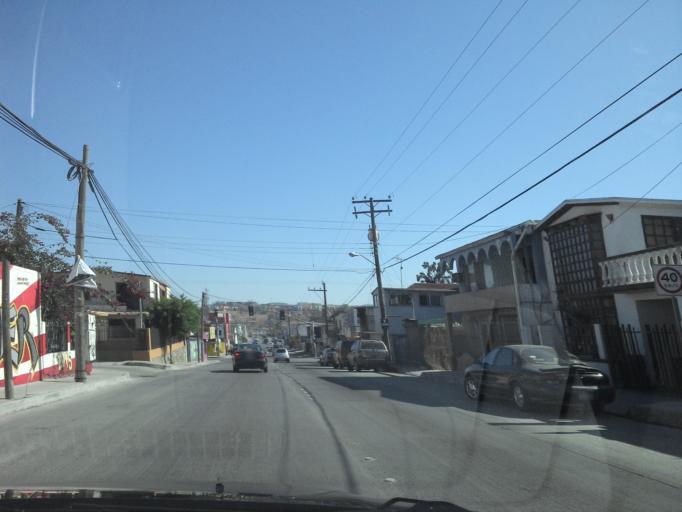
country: MX
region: Baja California
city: Tijuana
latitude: 32.5247
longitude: -116.9275
